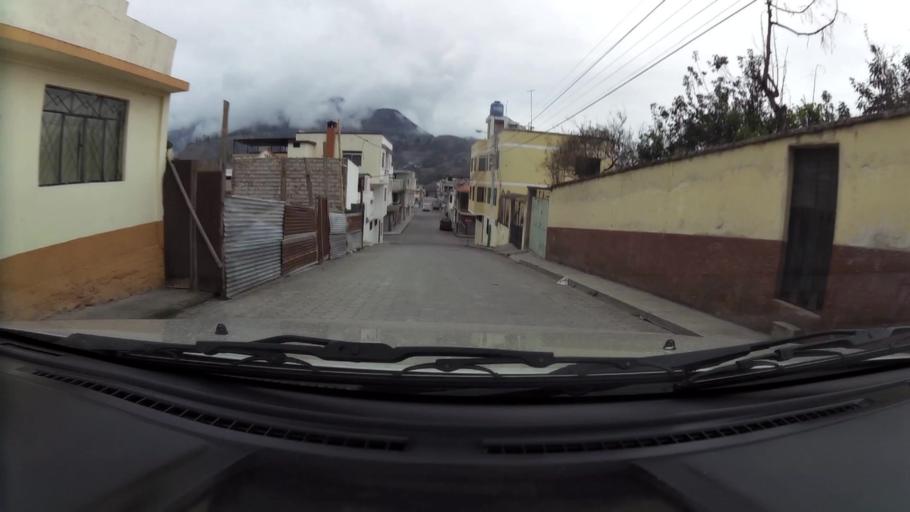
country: EC
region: Chimborazo
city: Alausi
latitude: -2.2892
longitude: -78.9214
